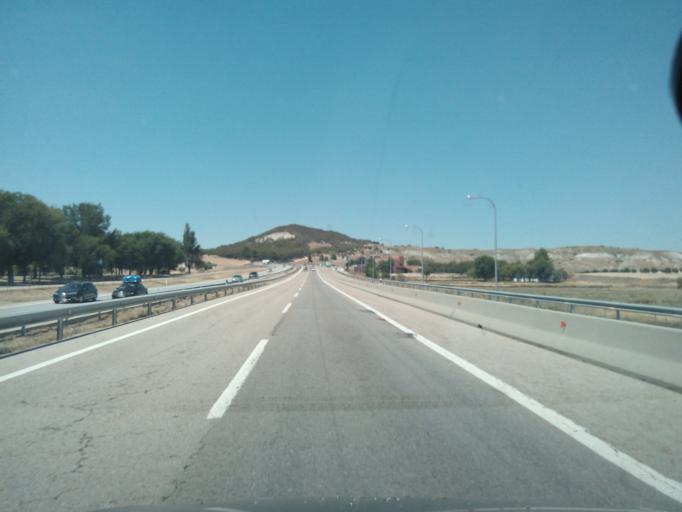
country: ES
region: Castille-La Mancha
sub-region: Province of Toledo
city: Dosbarrios
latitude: 39.8147
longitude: -3.4798
